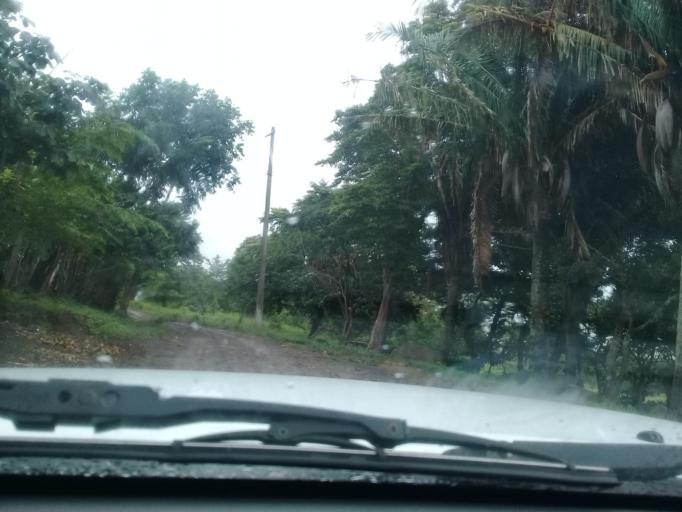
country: MX
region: Veracruz
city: Santiago Tuxtla
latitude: 18.4370
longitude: -95.2982
